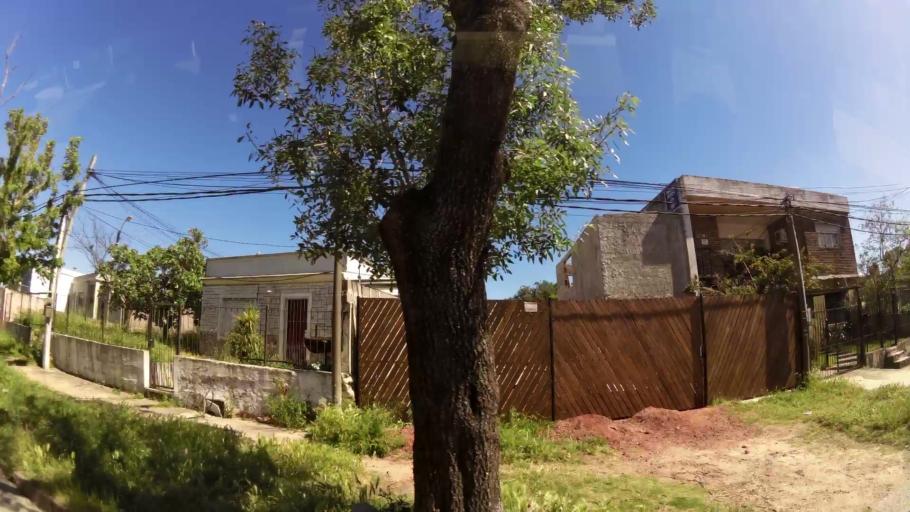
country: UY
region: Canelones
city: Paso de Carrasco
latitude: -34.8679
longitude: -56.1232
